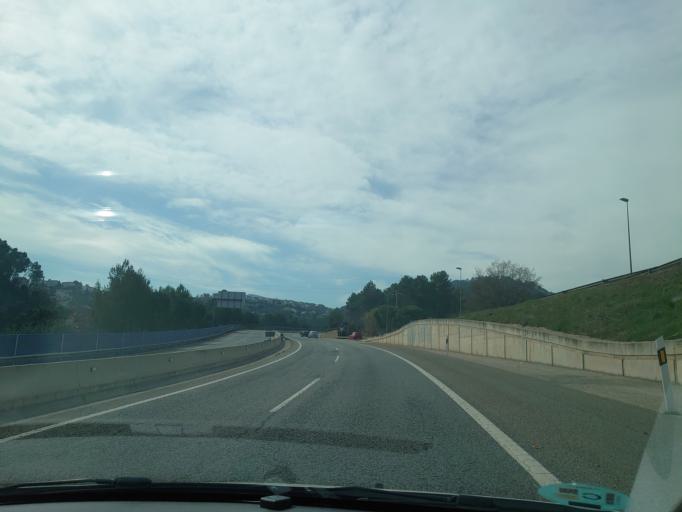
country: ES
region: Catalonia
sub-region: Provincia de Barcelona
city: Cervello
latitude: 41.3973
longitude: 1.9707
